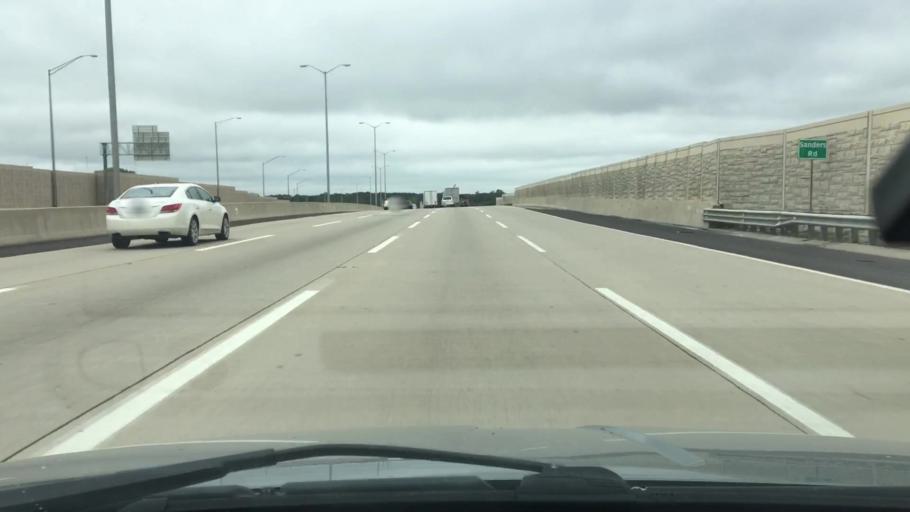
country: US
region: Illinois
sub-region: Lake County
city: Riverwoods
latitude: 42.1462
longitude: -87.8813
